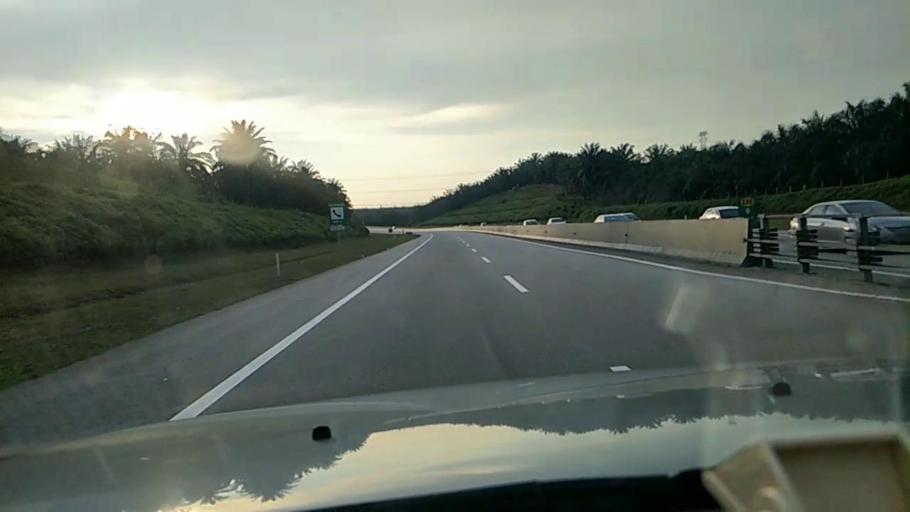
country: MY
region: Selangor
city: Batu Arang
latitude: 3.2859
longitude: 101.4398
